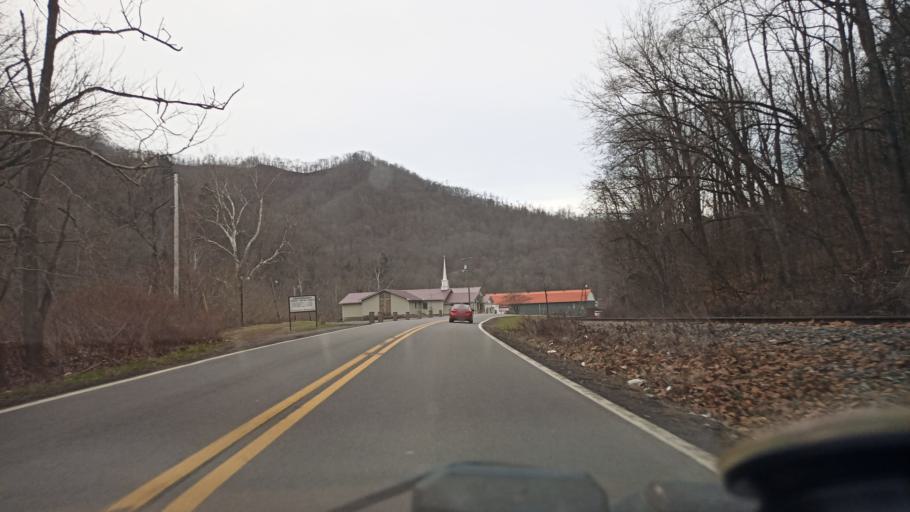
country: US
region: West Virginia
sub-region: Logan County
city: Mallory
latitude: 37.7251
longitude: -81.8747
